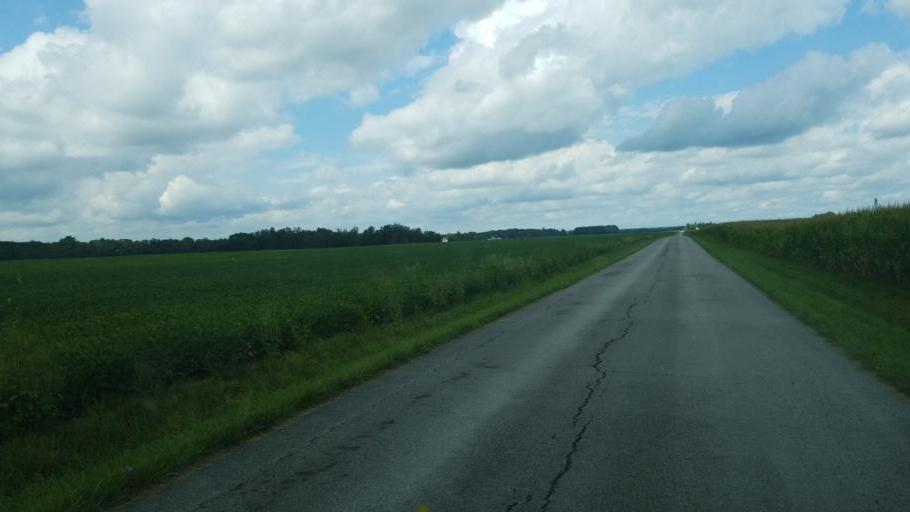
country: US
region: Ohio
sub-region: Huron County
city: Willard
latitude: 41.1443
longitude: -82.7562
